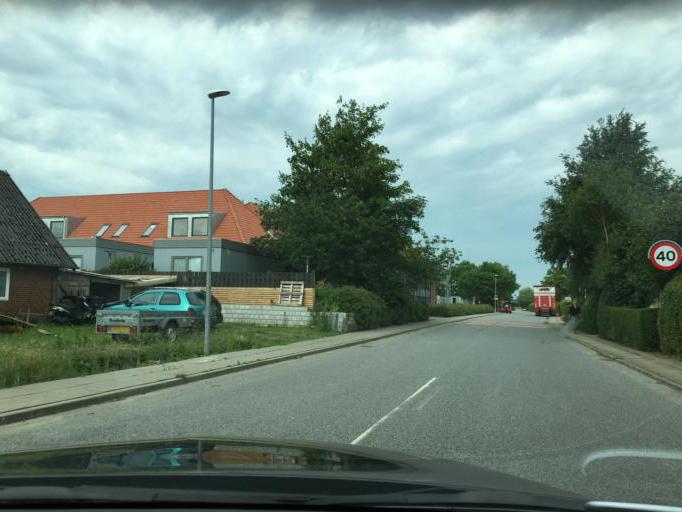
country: DK
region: South Denmark
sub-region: Fredericia Kommune
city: Taulov
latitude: 55.6142
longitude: 9.5671
